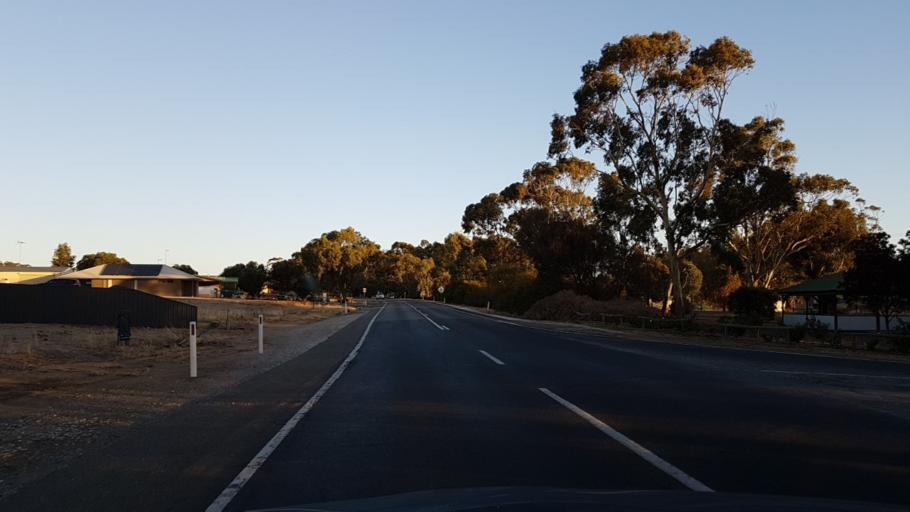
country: AU
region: South Australia
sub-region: Wakefield
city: Balaklava
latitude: -34.1485
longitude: 138.6901
